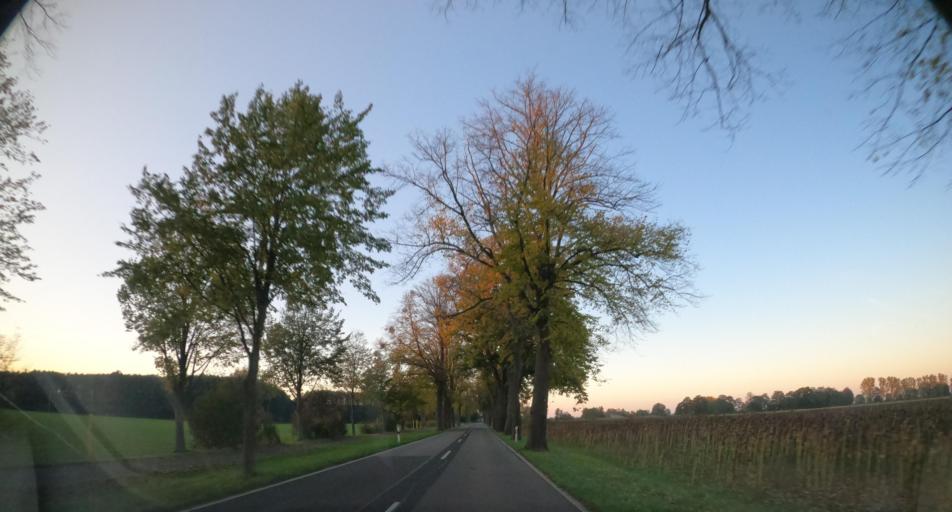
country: DE
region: Mecklenburg-Vorpommern
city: Ueckermunde
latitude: 53.7487
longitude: 14.0279
